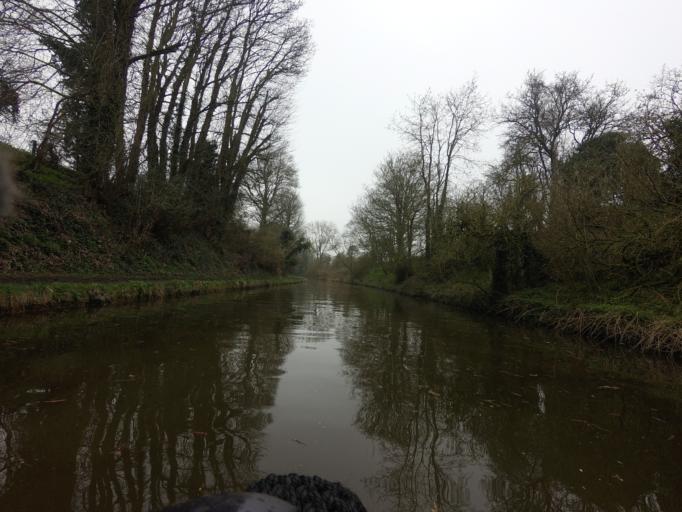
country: GB
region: England
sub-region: Hertfordshire
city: Tring
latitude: 51.7950
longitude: -0.6208
